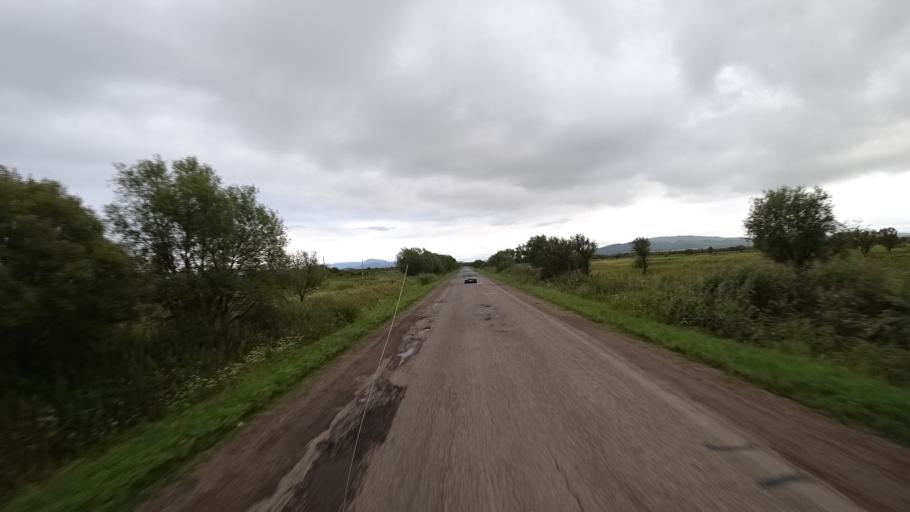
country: RU
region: Primorskiy
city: Chernigovka
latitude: 44.3609
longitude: 132.5554
